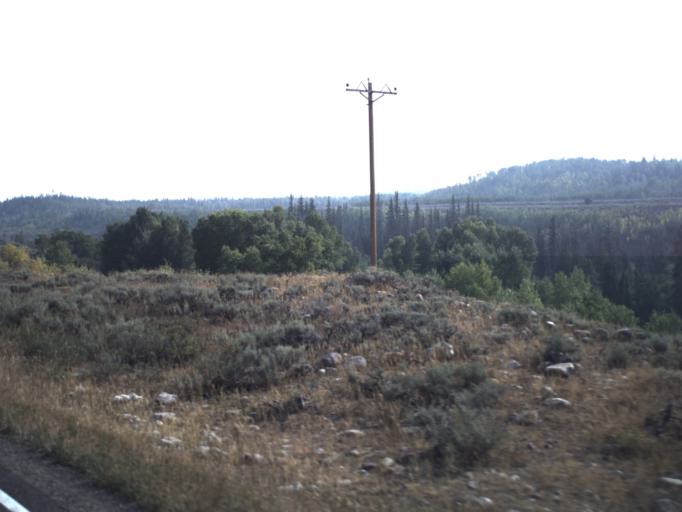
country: US
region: Wyoming
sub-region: Uinta County
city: Evanston
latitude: 40.9517
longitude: -110.8414
